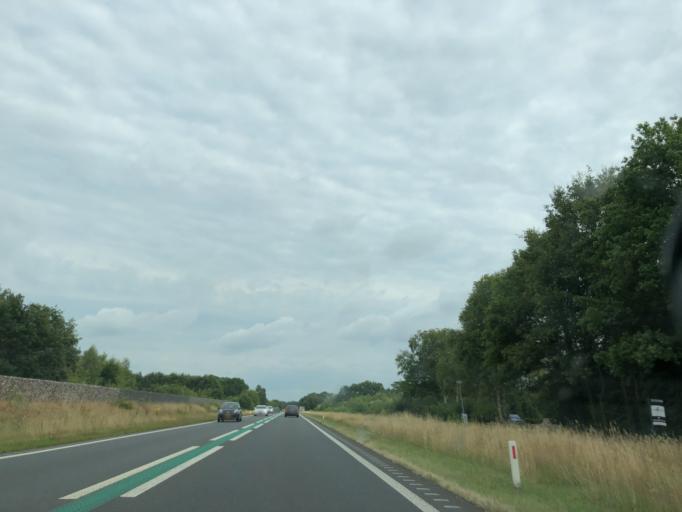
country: NL
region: Drenthe
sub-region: Gemeente Tynaarlo
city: Zuidlaren
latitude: 53.0759
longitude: 6.6798
